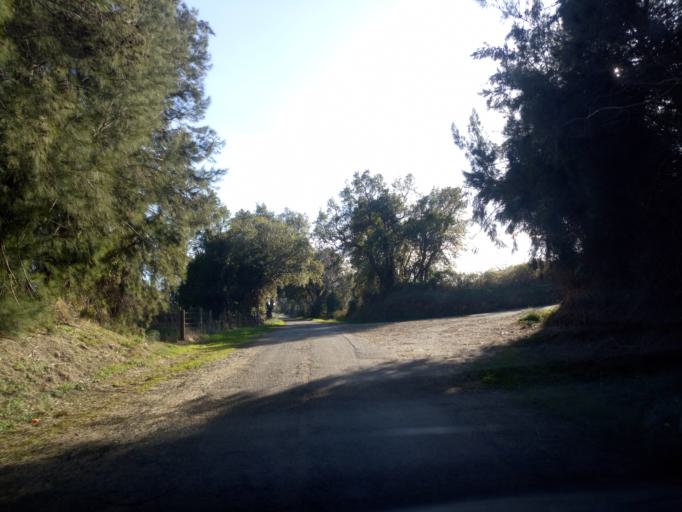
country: FR
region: Corsica
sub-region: Departement de la Haute-Corse
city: Linguizzetta
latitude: 42.2652
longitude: 9.5440
